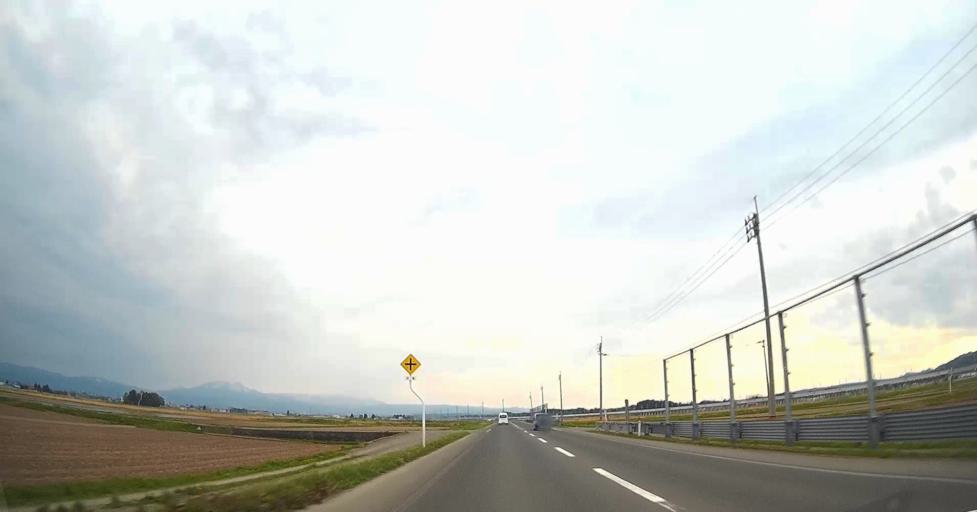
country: JP
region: Aomori
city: Aomori Shi
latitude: 40.8804
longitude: 140.6707
